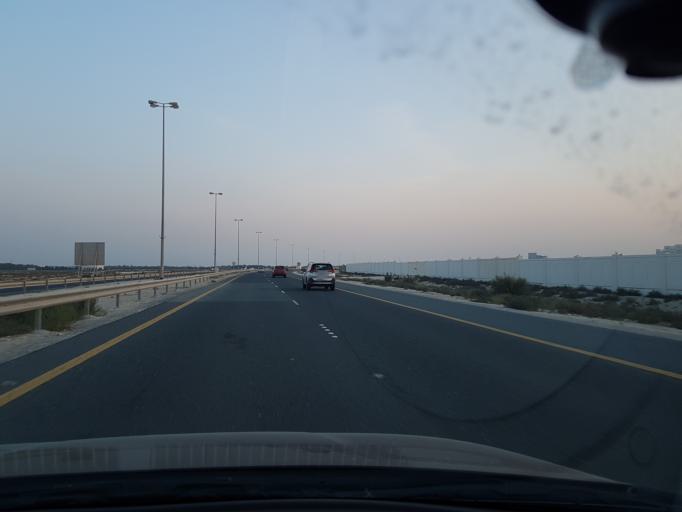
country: BH
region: Central Governorate
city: Dar Kulayb
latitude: 26.0352
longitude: 50.4998
